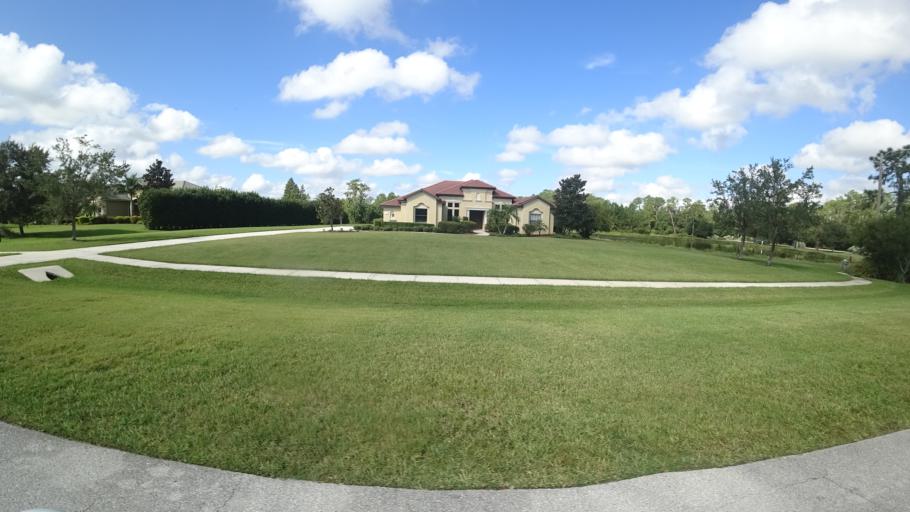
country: US
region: Florida
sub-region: Sarasota County
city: Fruitville
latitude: 27.3989
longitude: -82.3097
